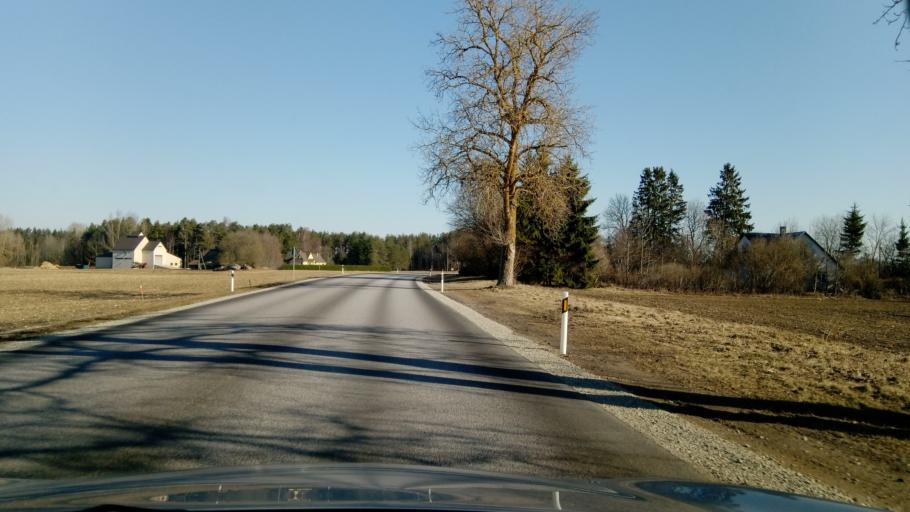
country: EE
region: Laeaene-Virumaa
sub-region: Rakvere linn
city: Rakvere
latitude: 59.2713
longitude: 26.2846
